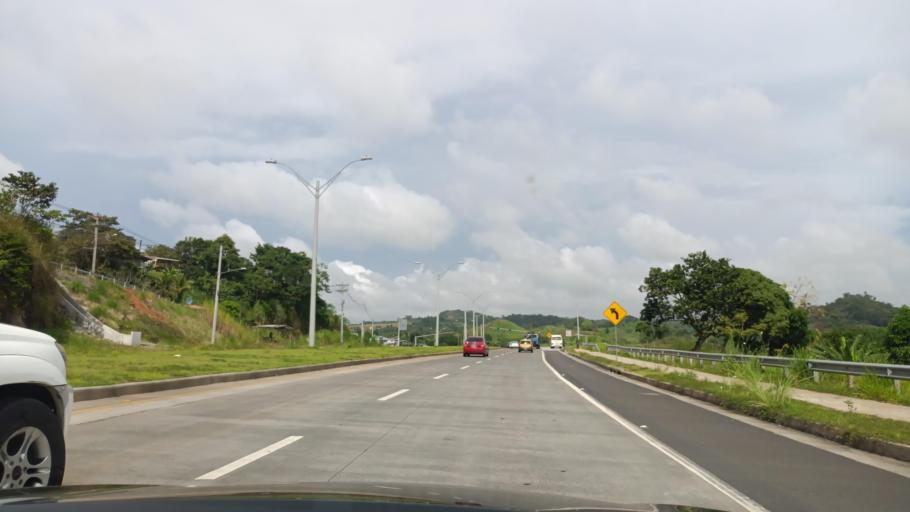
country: PA
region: Panama
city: Las Cumbres
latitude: 9.0976
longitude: -79.4875
